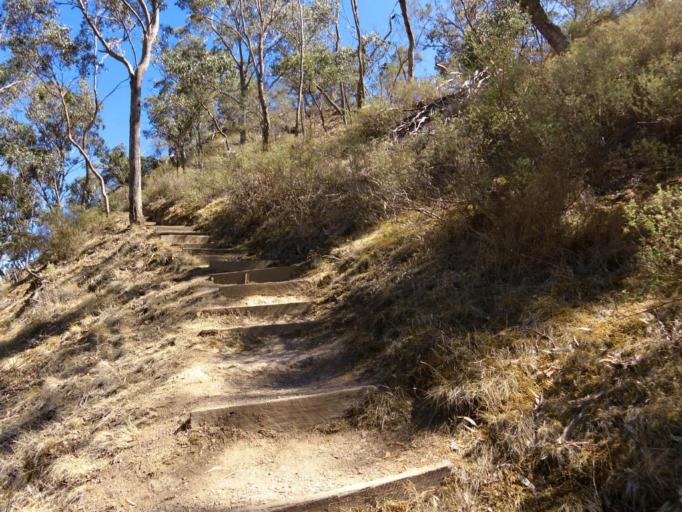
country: AU
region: Victoria
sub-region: Moorabool
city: Bacchus Marsh
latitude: -37.6716
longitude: 144.3615
